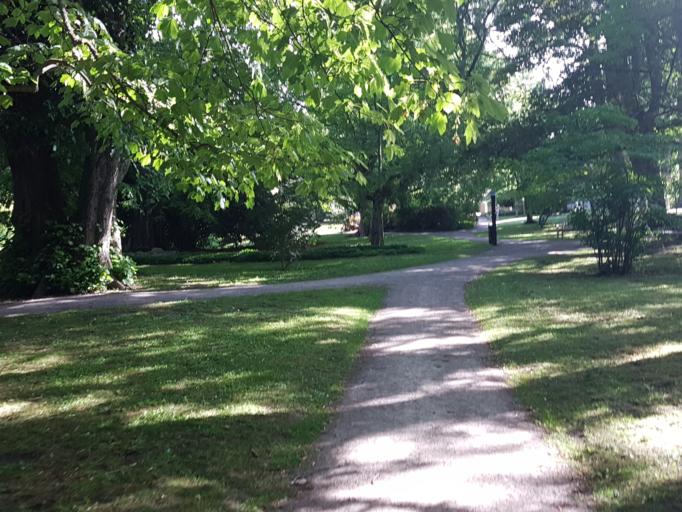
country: SE
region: Gotland
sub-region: Gotland
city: Visby
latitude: 57.6440
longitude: 18.2935
